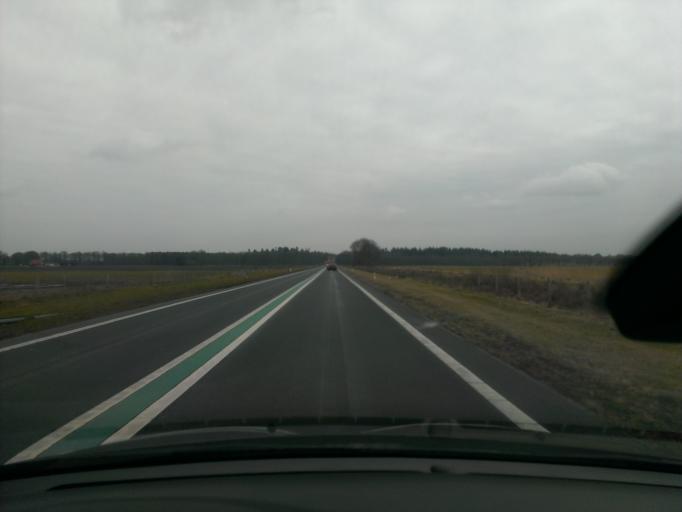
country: NL
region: Overijssel
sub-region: Gemeente Twenterand
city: Magele
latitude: 52.5599
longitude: 6.5093
